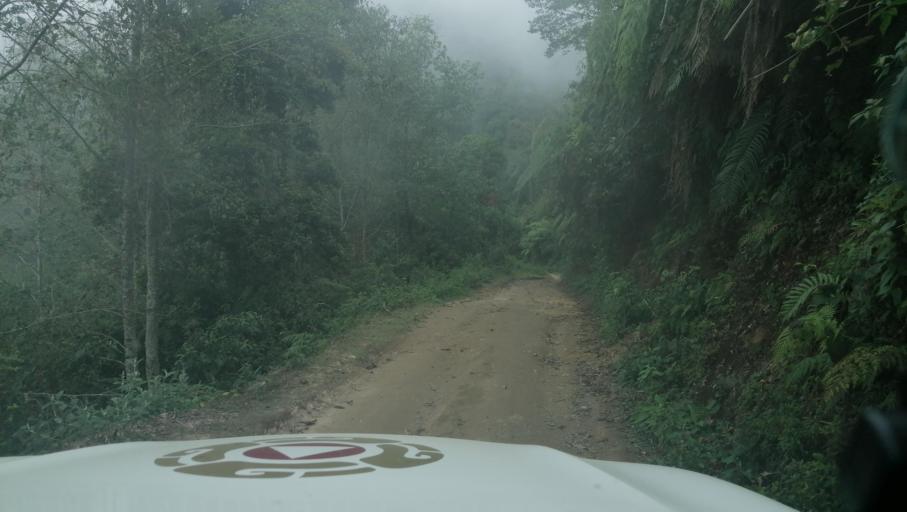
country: GT
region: San Marcos
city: Tacana
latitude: 15.2164
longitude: -92.1836
